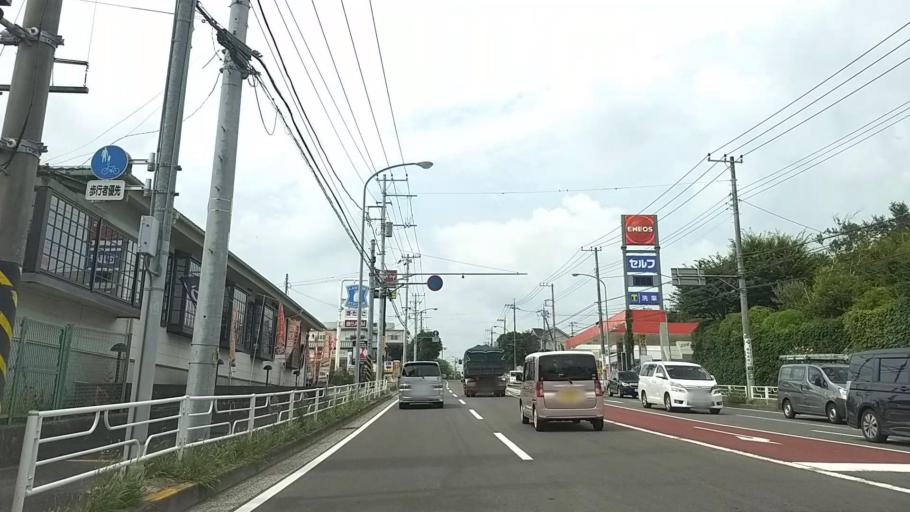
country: JP
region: Kanagawa
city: Minami-rinkan
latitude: 35.4963
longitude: 139.5360
